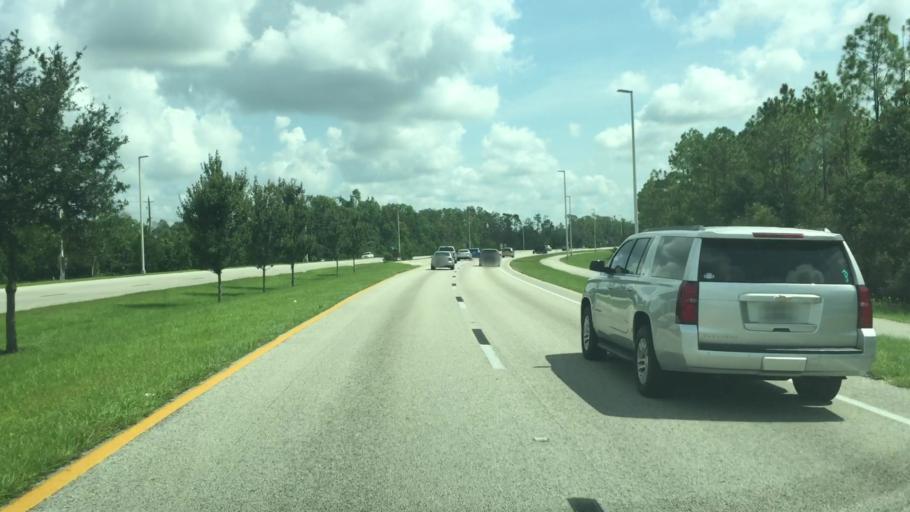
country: US
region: Florida
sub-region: Lee County
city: Villas
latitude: 26.5501
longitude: -81.8389
